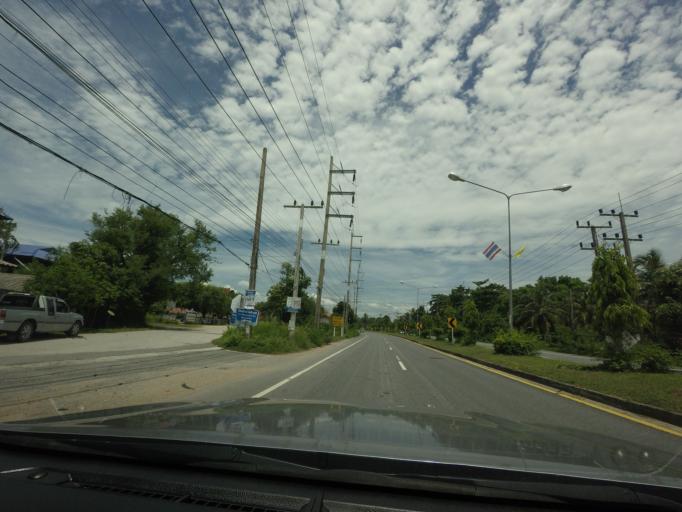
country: TH
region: Songkhla
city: Sathing Phra
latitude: 7.5537
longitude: 100.4142
